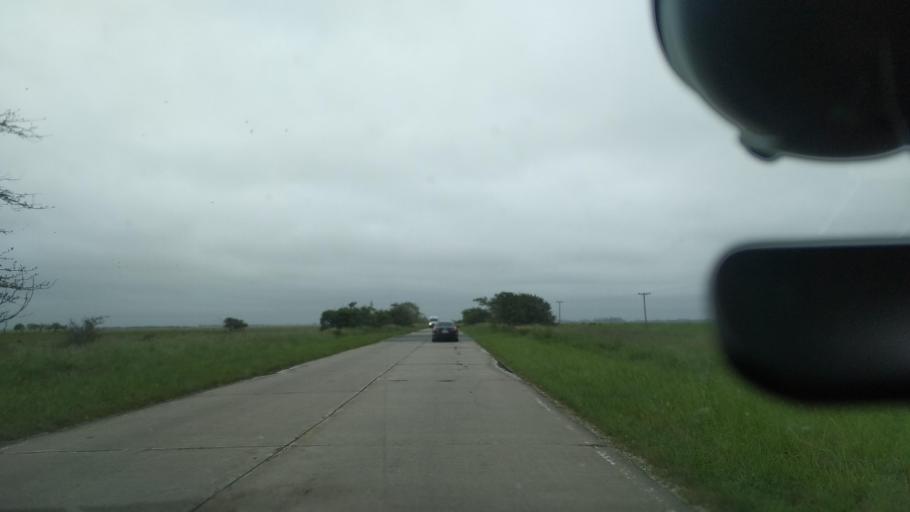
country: AR
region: Buenos Aires
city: Veronica
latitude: -35.5721
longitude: -57.2851
